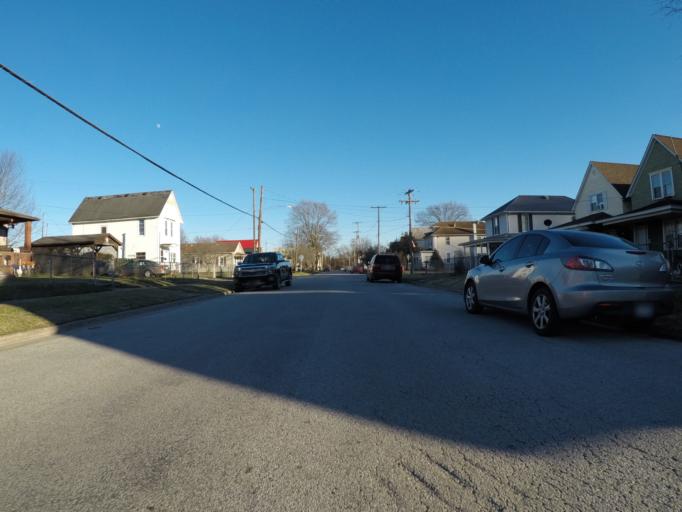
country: US
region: West Virginia
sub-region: Wayne County
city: Kenova
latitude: 38.3985
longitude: -82.5820
